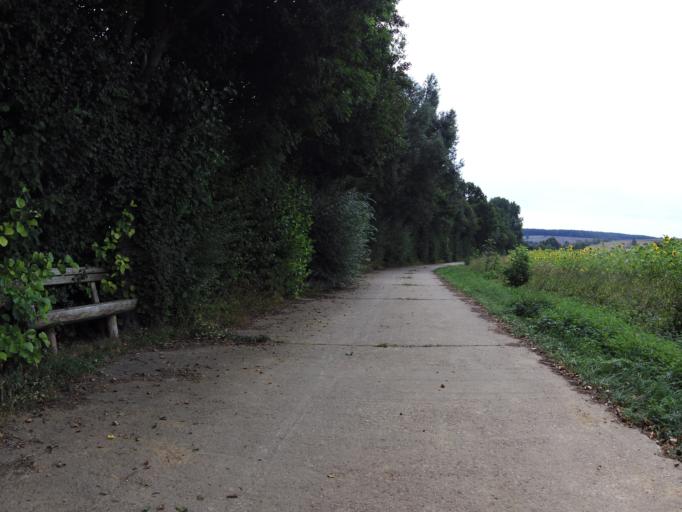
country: DE
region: Bavaria
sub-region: Regierungsbezirk Unterfranken
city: Kleinrinderfeld
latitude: 49.7055
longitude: 9.8367
